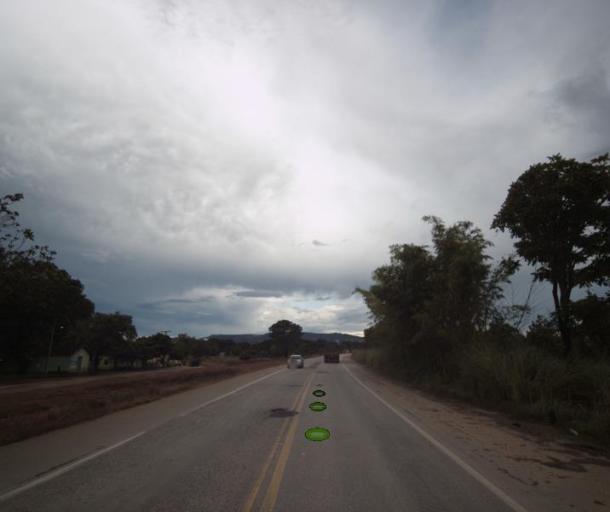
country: BR
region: Goias
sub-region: Porangatu
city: Porangatu
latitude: -13.5759
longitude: -49.0430
